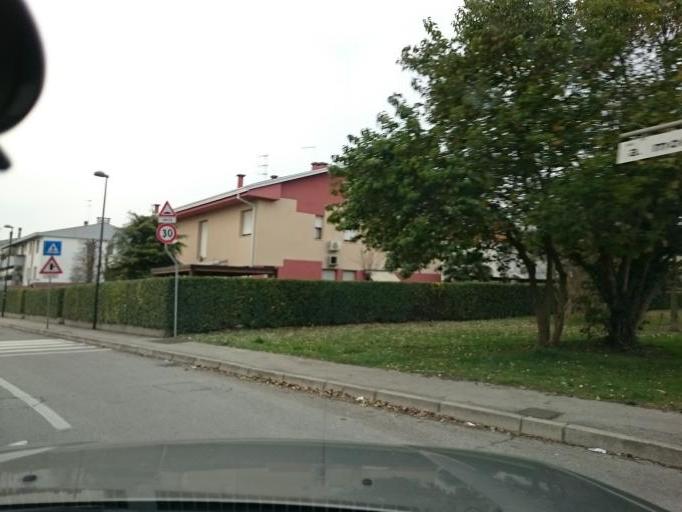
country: IT
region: Veneto
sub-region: Provincia di Padova
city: Ponte San Nicolo
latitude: 45.3653
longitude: 11.9294
